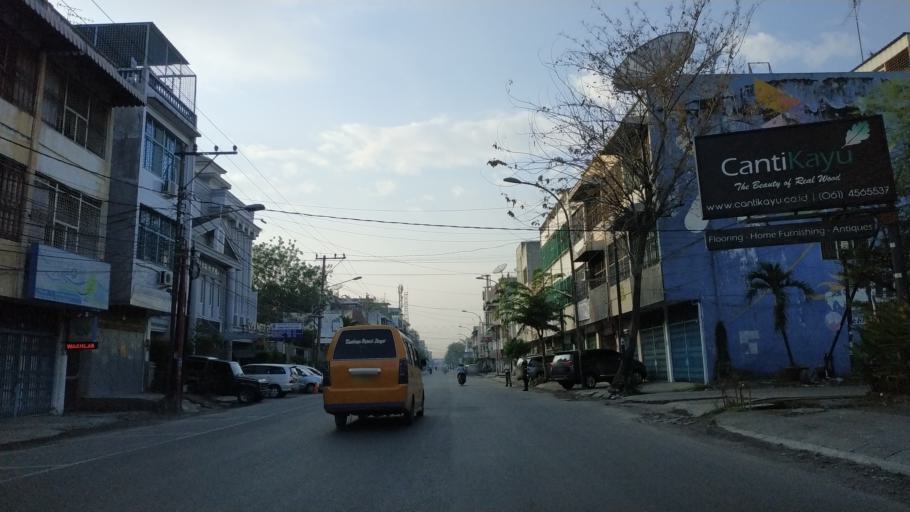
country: ID
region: North Sumatra
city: Medan
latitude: 3.5949
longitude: 98.6881
